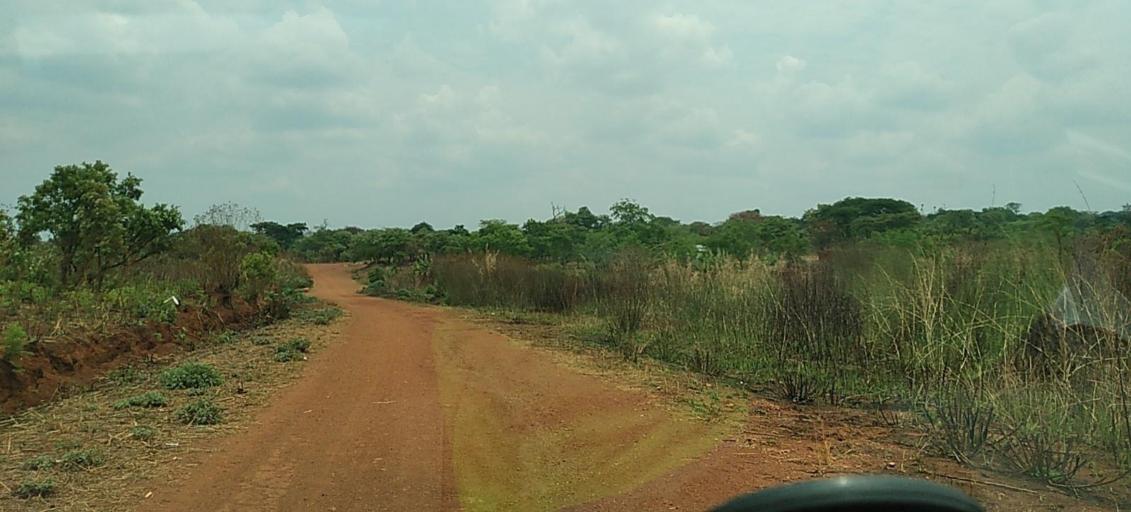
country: ZM
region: North-Western
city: Kansanshi
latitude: -12.0435
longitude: 26.3893
